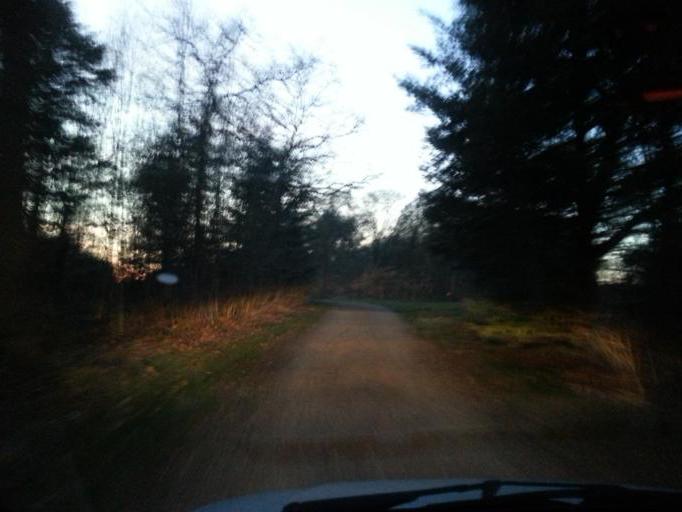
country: DK
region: South Denmark
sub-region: Esbjerg Kommune
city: Esbjerg
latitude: 55.4997
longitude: 8.4385
